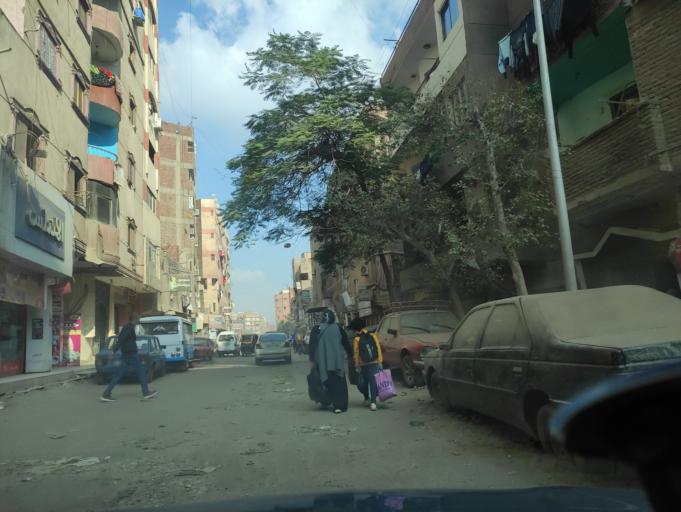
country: EG
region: Muhafazat al Qahirah
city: Cairo
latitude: 30.1258
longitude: 31.3056
